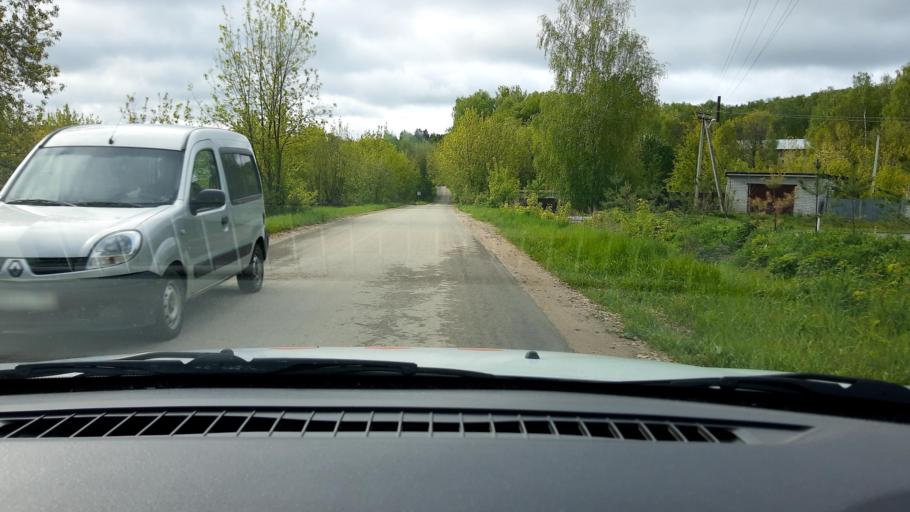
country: RU
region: Nizjnij Novgorod
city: Afonino
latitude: 56.1909
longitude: 44.0737
